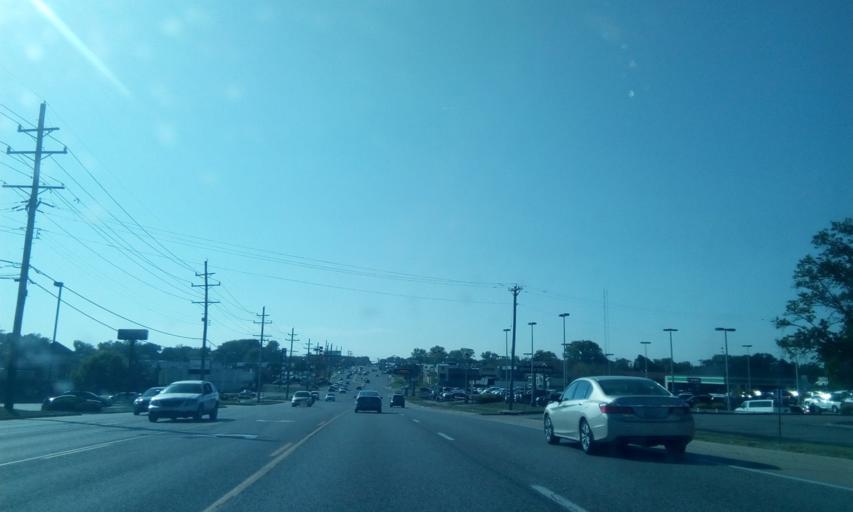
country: US
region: Missouri
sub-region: Saint Louis County
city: Concord
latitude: 38.5227
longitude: -90.3490
